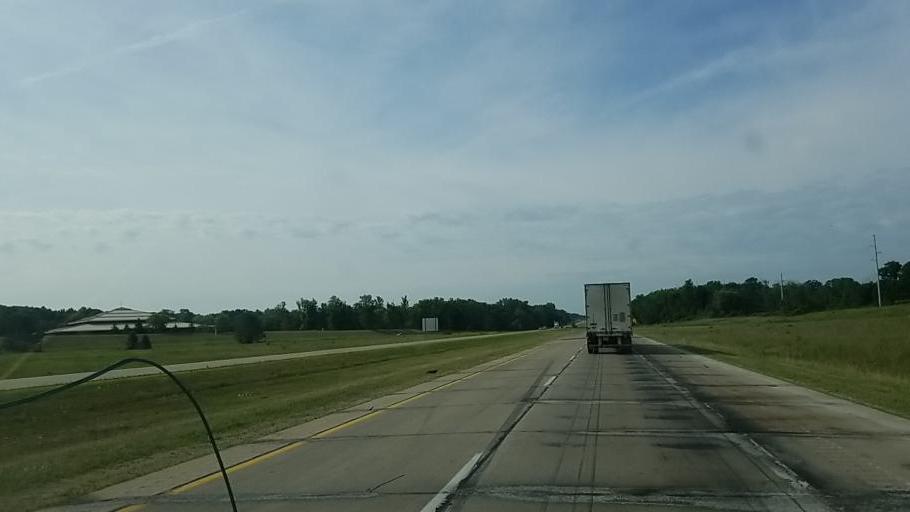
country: US
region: Michigan
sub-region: Eaton County
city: Charlotte
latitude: 42.5527
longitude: -84.8212
